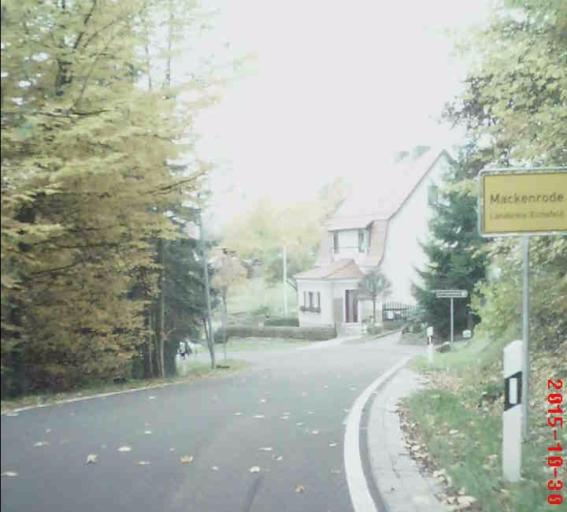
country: DE
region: Thuringia
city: Mackenrode
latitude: 51.3051
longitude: 10.0720
